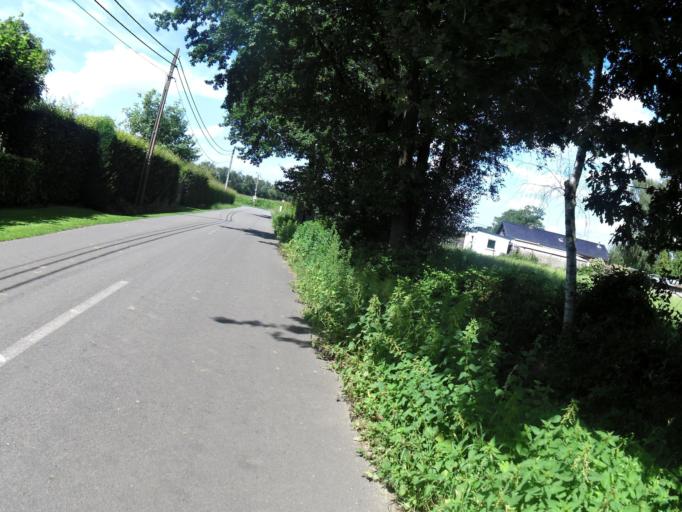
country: BE
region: Flanders
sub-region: Provincie Antwerpen
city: Geel
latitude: 51.1513
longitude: 4.9469
